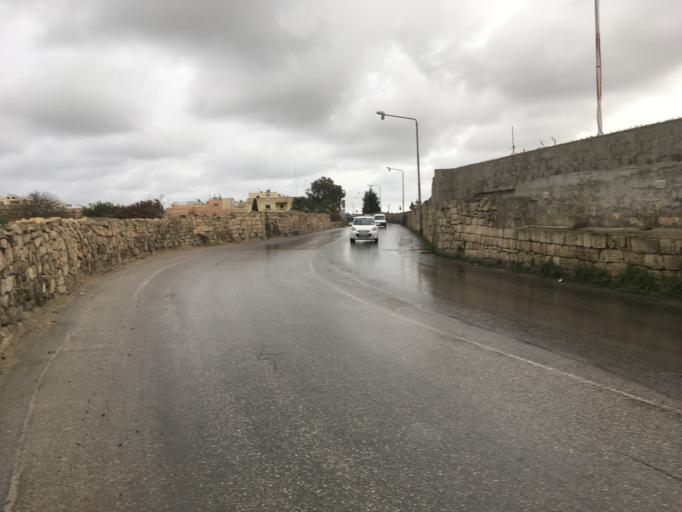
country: MT
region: Hal Gharghur
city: Hal Gharghur
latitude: 35.9164
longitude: 14.4511
